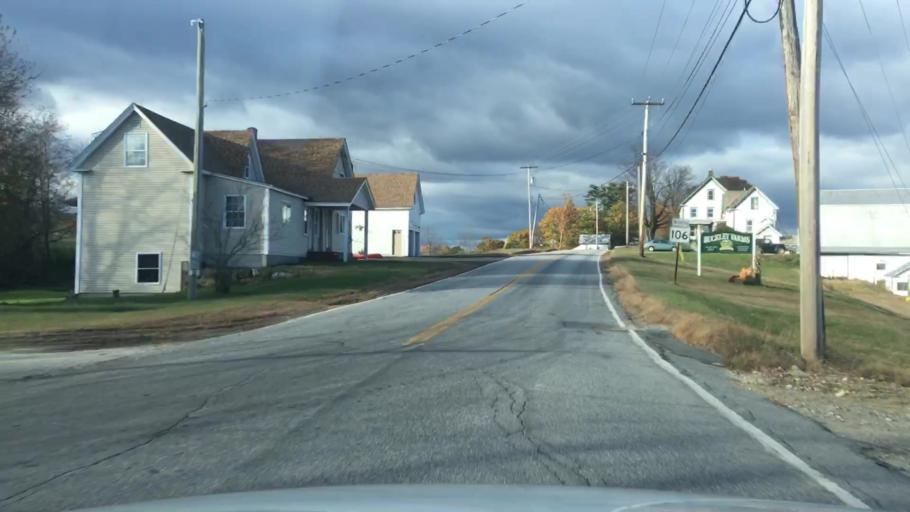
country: US
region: Maine
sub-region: Androscoggin County
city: Leeds
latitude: 44.3035
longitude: -70.1192
